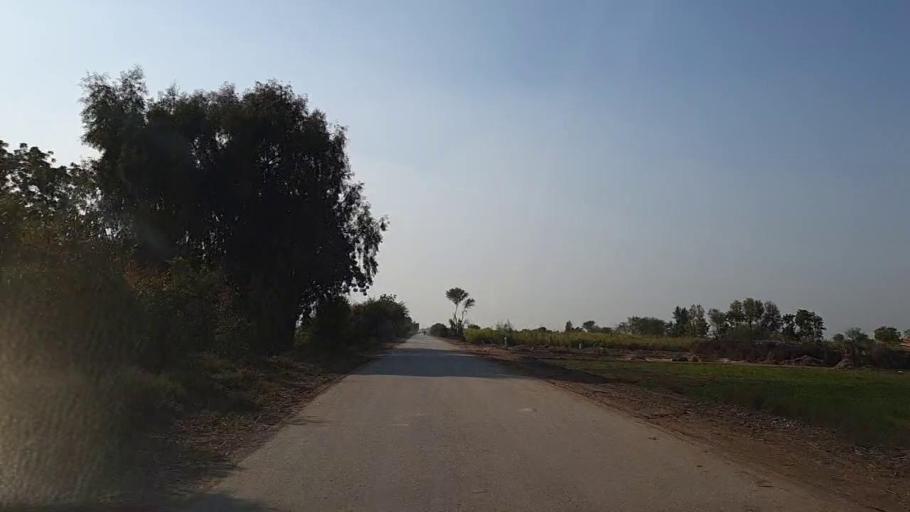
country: PK
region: Sindh
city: Daur
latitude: 26.4040
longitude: 68.2794
